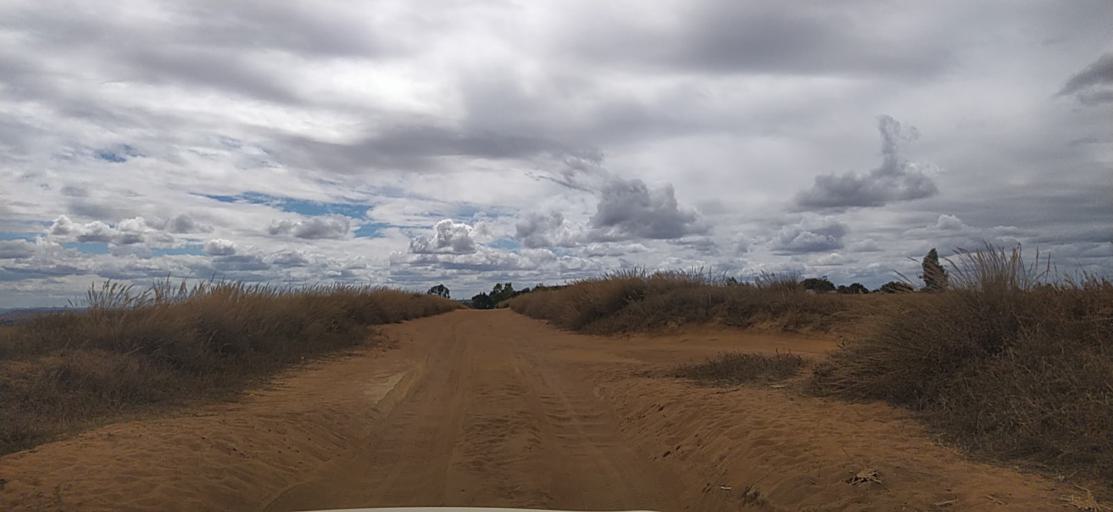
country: MG
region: Alaotra Mangoro
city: Ambatondrazaka
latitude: -17.9026
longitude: 48.2582
